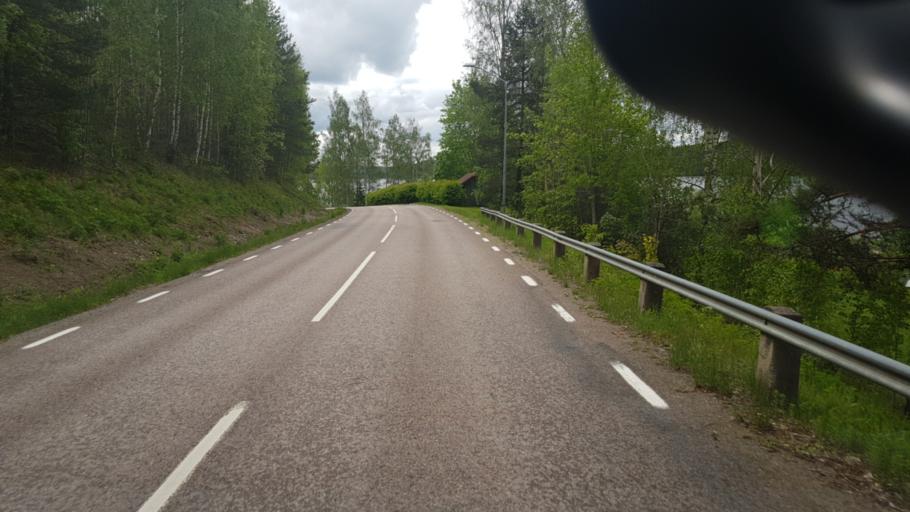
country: SE
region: Vaermland
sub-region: Arvika Kommun
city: Arvika
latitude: 59.8446
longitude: 12.5520
